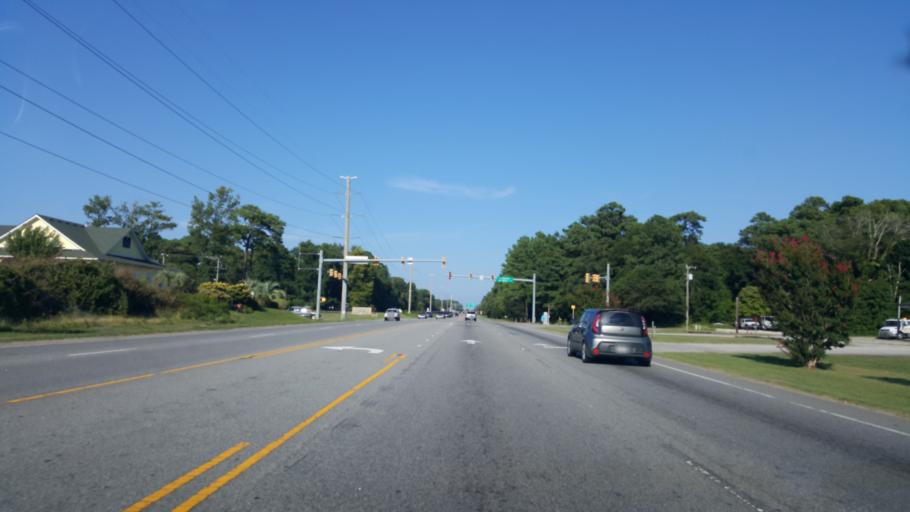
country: US
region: North Carolina
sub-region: Dare County
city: Kitty Hawk
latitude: 36.0954
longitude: -75.7340
